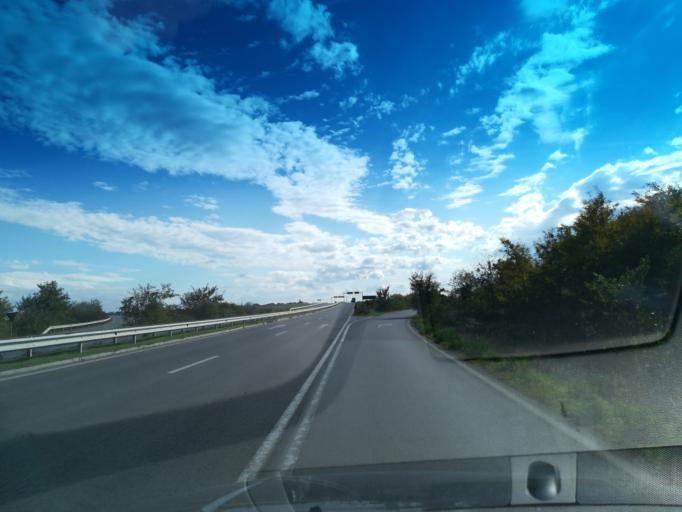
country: BG
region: Stara Zagora
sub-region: Obshtina Stara Zagora
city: Stara Zagora
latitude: 42.3430
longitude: 25.6608
